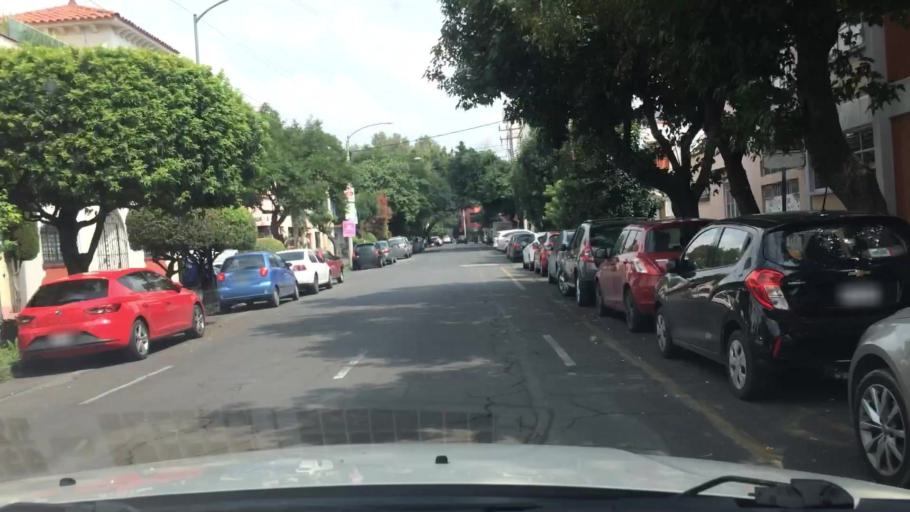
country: MX
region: Mexico City
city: Benito Juarez
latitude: 19.3996
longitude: -99.1641
